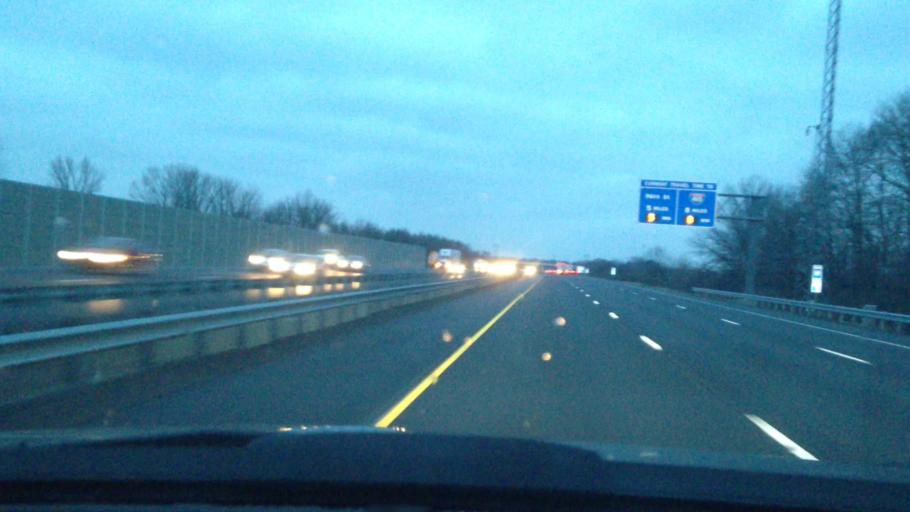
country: US
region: Indiana
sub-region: Hamilton County
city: Fishers
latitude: 39.9762
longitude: -85.9588
